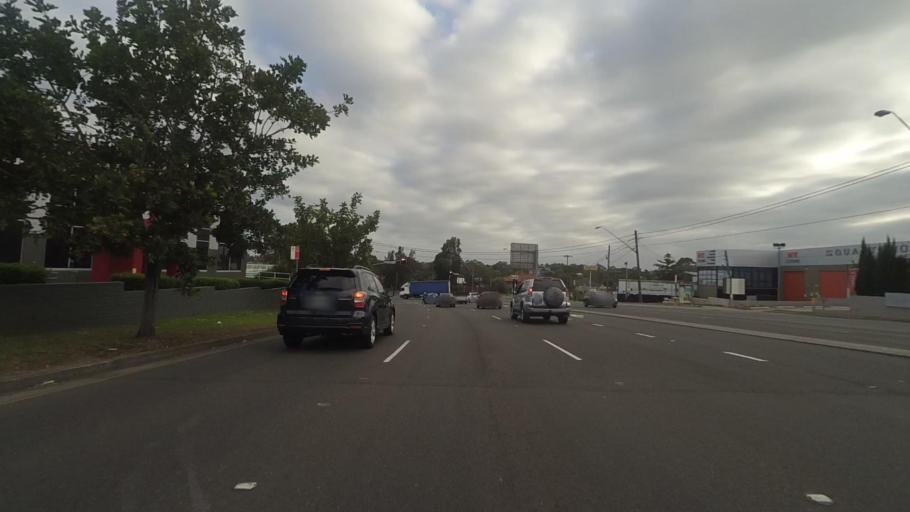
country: AU
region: New South Wales
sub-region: Bankstown
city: Padstow
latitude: -33.9443
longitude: 151.0348
